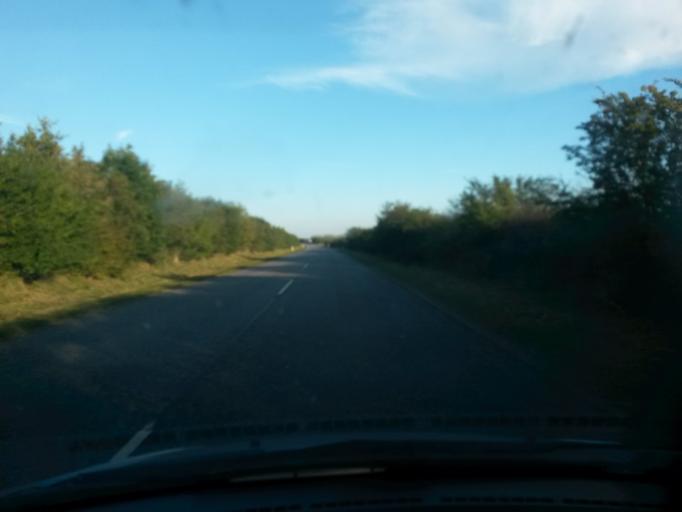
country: DK
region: Central Jutland
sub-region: Silkeborg Kommune
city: Kjellerup
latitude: 56.3016
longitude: 9.3107
